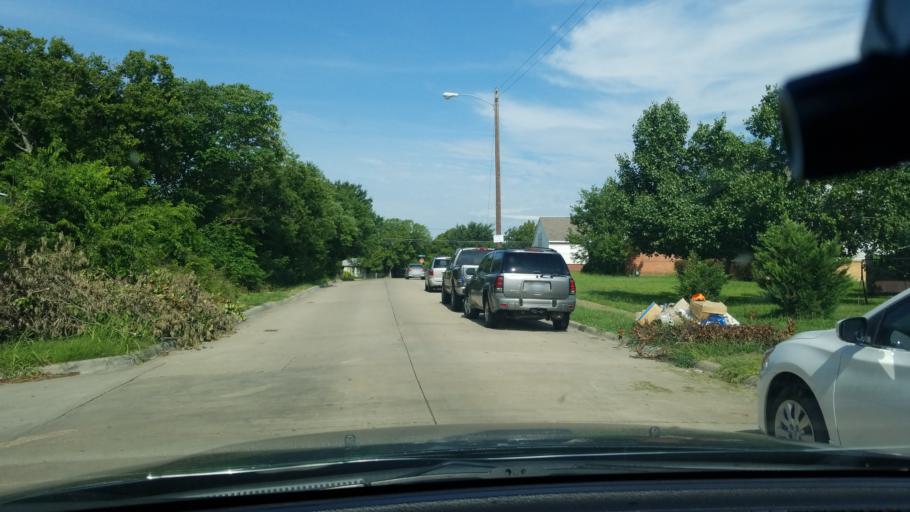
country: US
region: Texas
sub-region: Dallas County
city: Balch Springs
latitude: 32.7300
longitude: -96.6471
